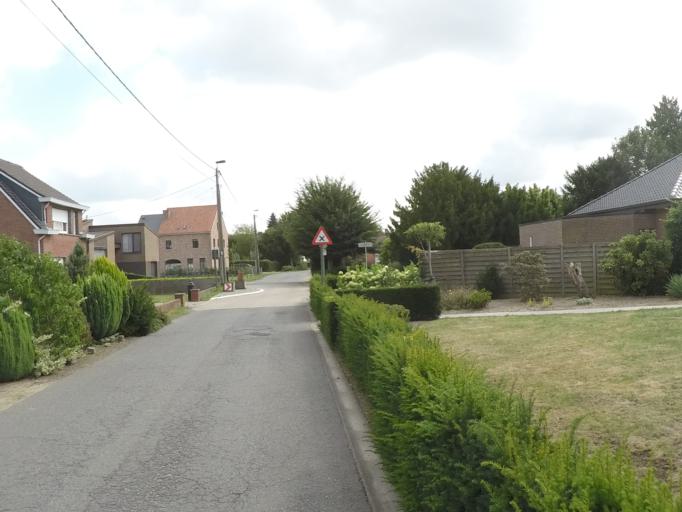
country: BE
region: Flanders
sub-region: Provincie Antwerpen
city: Ranst
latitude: 51.1851
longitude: 4.5942
